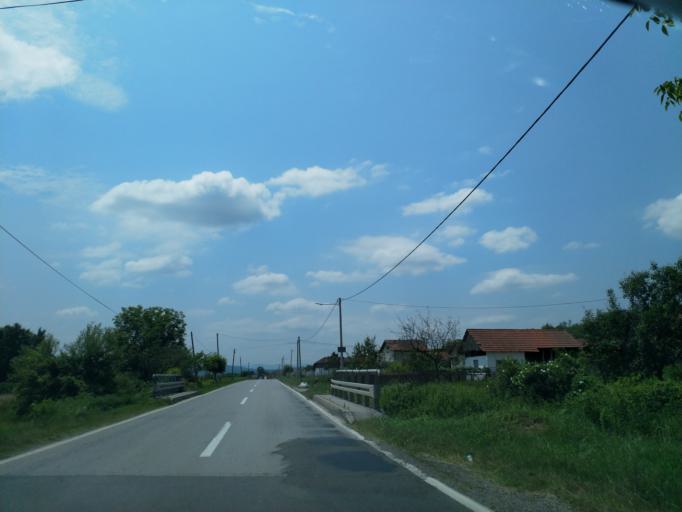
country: RS
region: Central Serbia
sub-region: Rasinski Okrug
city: Krusevac
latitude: 43.4735
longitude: 21.2602
